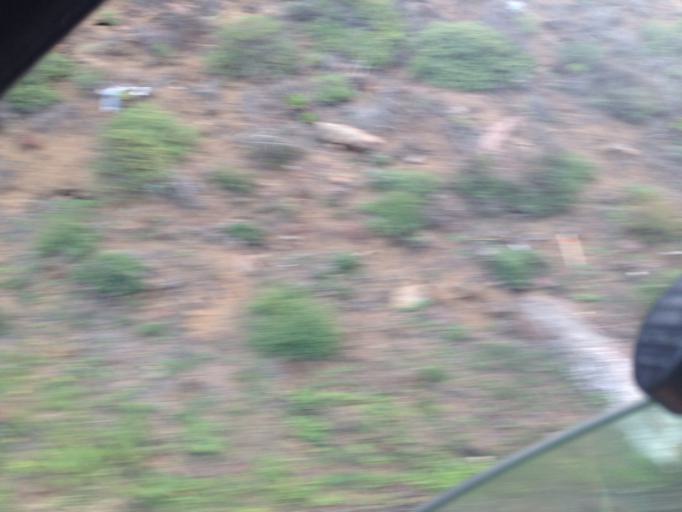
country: MX
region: Baja California
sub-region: Playas de Rosarito
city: Santa Anita
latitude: 32.1016
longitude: -116.8823
